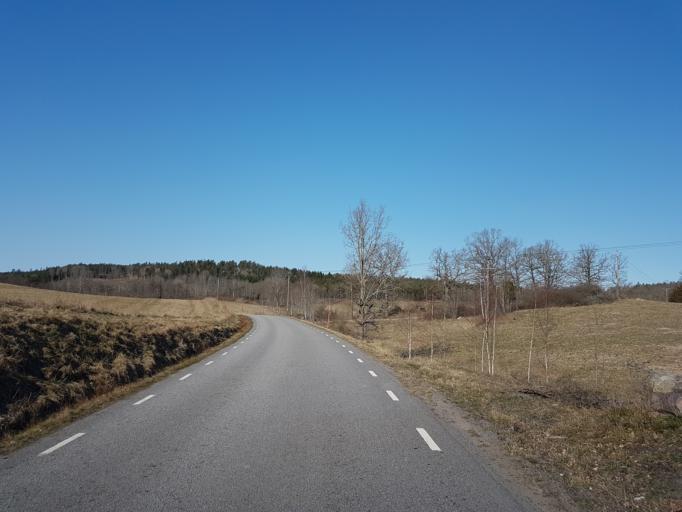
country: SE
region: OEstergoetland
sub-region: Valdemarsviks Kommun
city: Gusum
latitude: 58.2005
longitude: 16.3528
